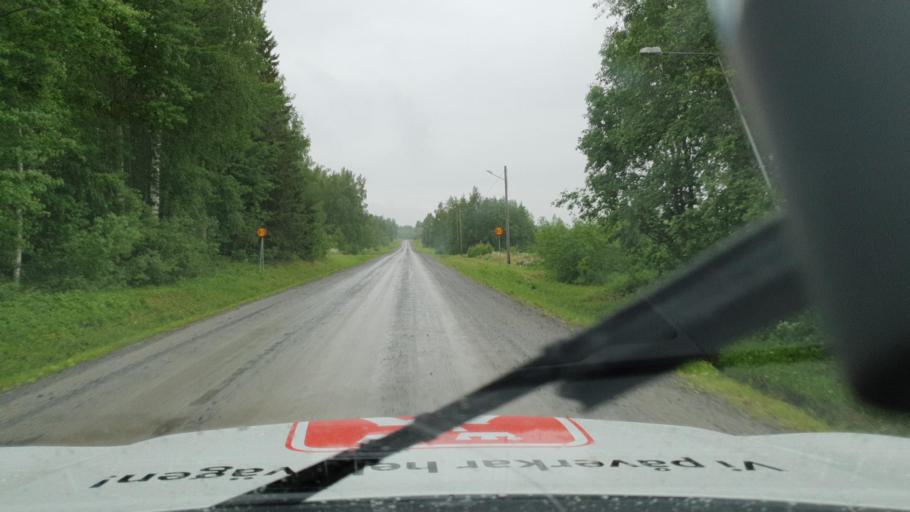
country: SE
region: Vaesterbotten
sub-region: Bjurholms Kommun
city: Bjurholm
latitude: 63.8662
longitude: 19.4631
